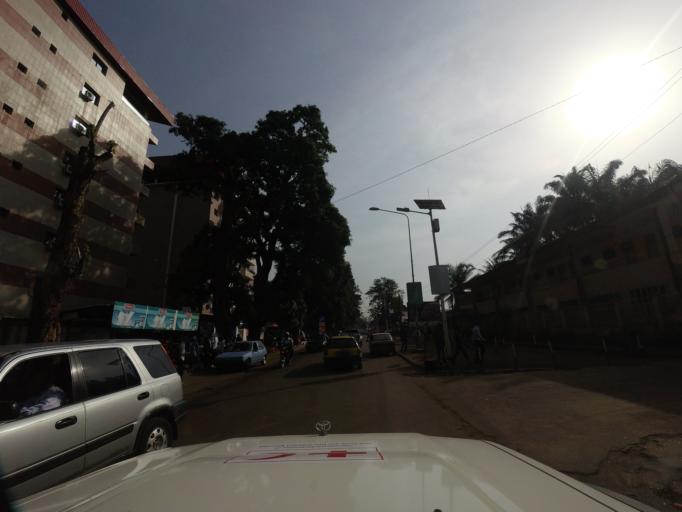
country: GN
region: Conakry
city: Conakry
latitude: 9.5420
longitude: -13.6806
